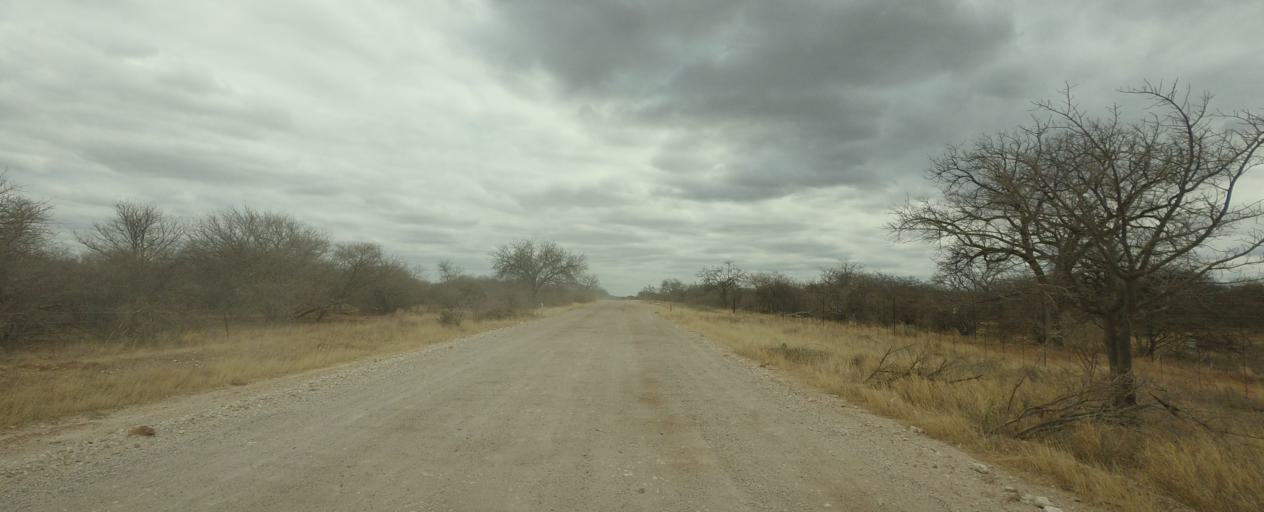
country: BW
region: Central
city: Mogapi
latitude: -22.7806
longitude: 28.3188
